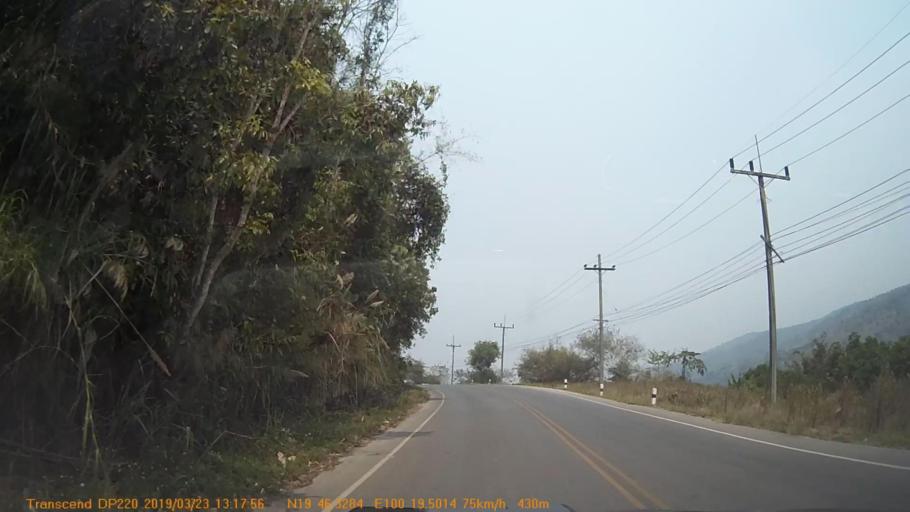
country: TH
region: Chiang Rai
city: Khun Tan
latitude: 19.7724
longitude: 100.3252
